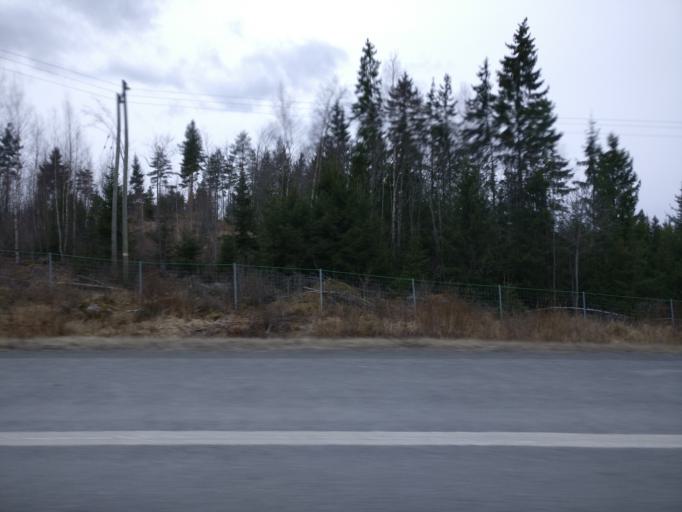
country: FI
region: Pirkanmaa
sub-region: Etelae-Pirkanmaa
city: Toijala
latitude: 61.1990
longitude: 23.8464
